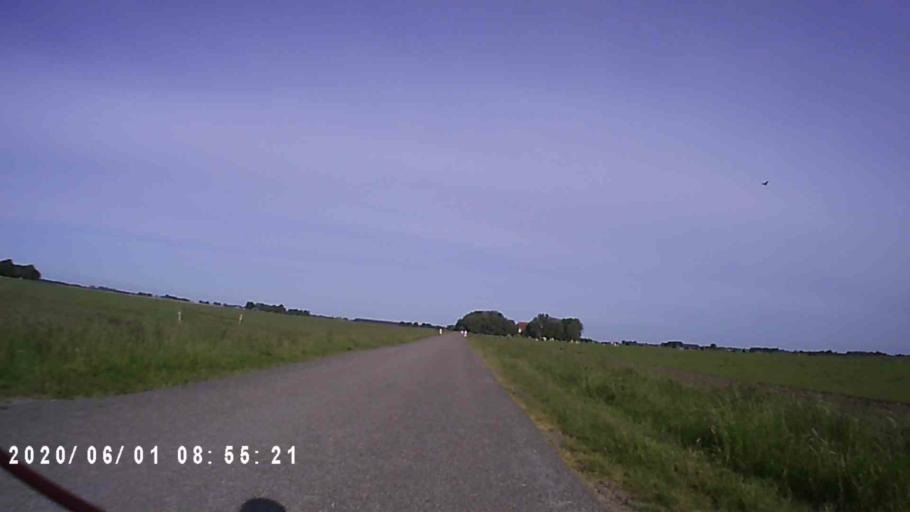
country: NL
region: Friesland
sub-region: Gemeente Leeuwarderadeel
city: Britsum
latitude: 53.2783
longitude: 5.8248
